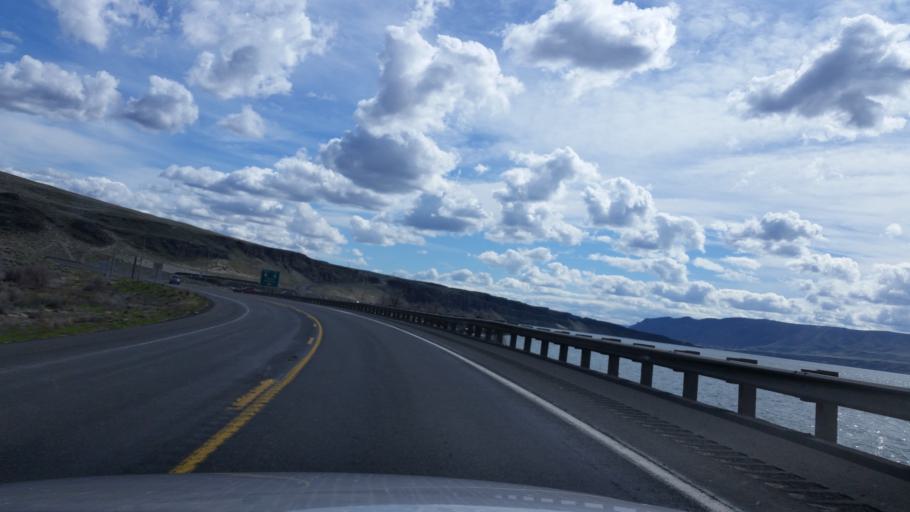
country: US
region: Washington
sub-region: Grant County
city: Mattawa
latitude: 46.9323
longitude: -119.9585
